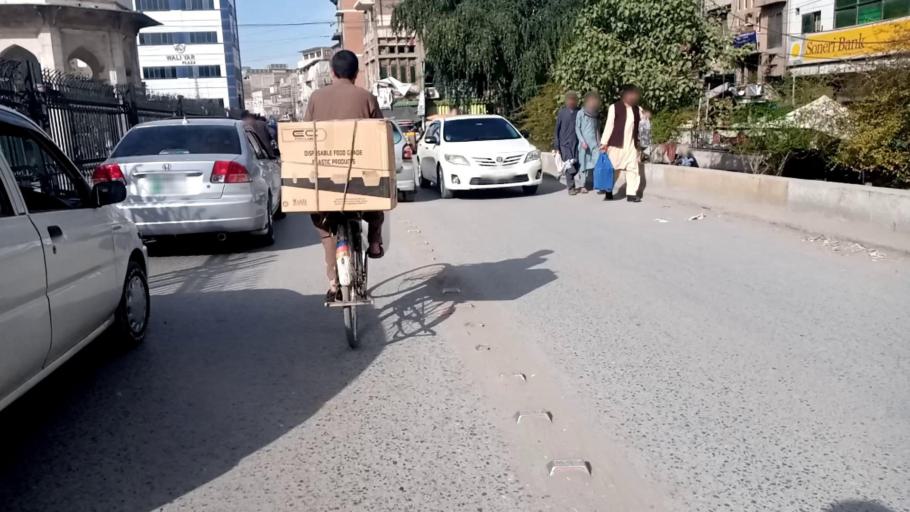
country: PK
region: Khyber Pakhtunkhwa
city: Peshawar
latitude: 34.0097
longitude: 71.5742
